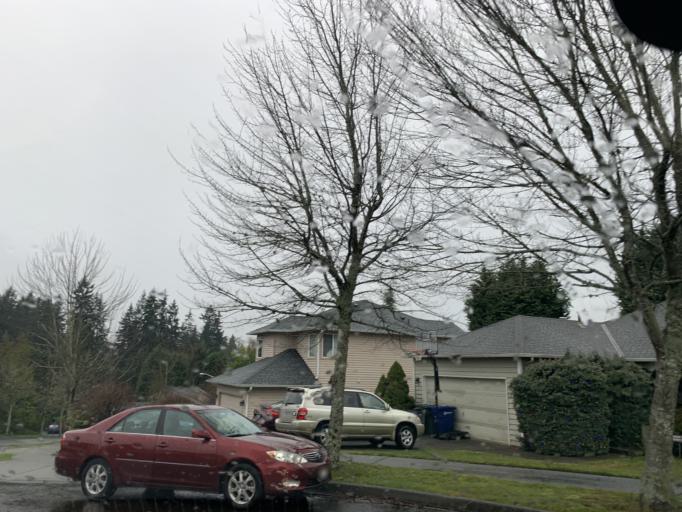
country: US
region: Washington
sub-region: King County
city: Woodinville
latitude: 47.7479
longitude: -122.1766
